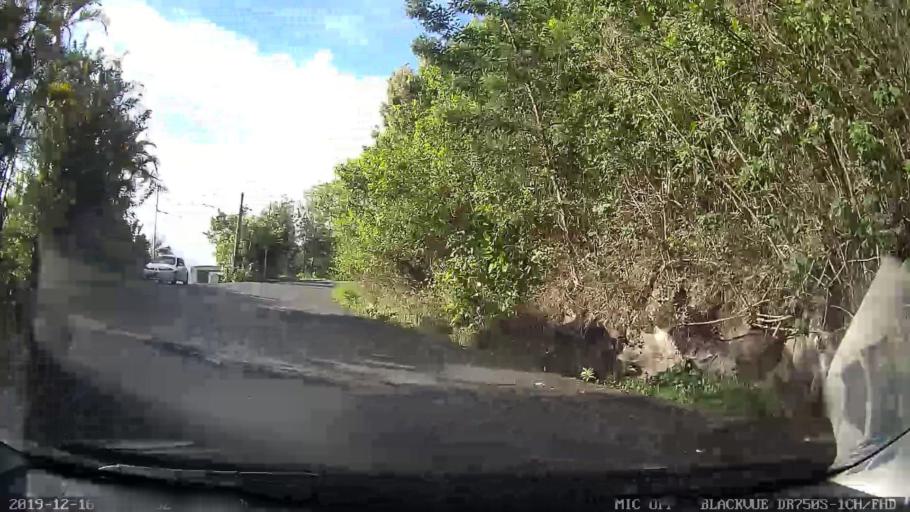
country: RE
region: Reunion
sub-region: Reunion
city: Le Tampon
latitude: -21.2607
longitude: 55.5090
